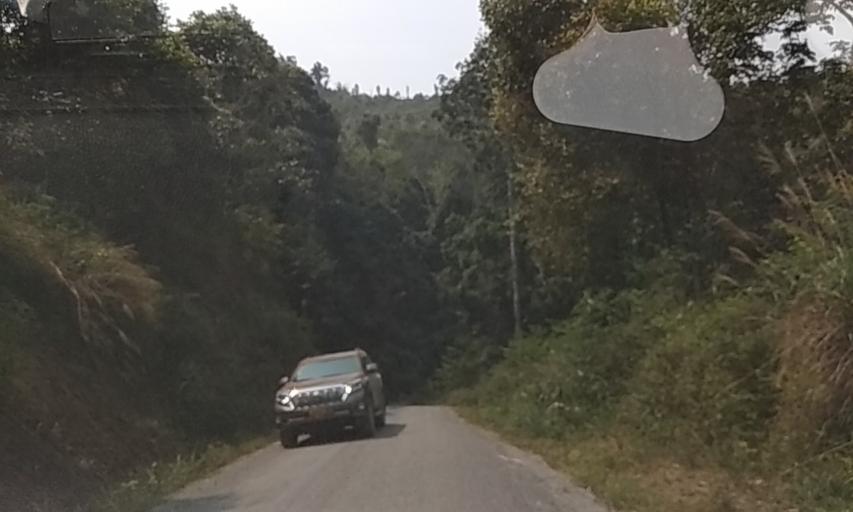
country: TH
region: Nan
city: Chaloem Phra Kiat
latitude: 20.0511
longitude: 101.0759
